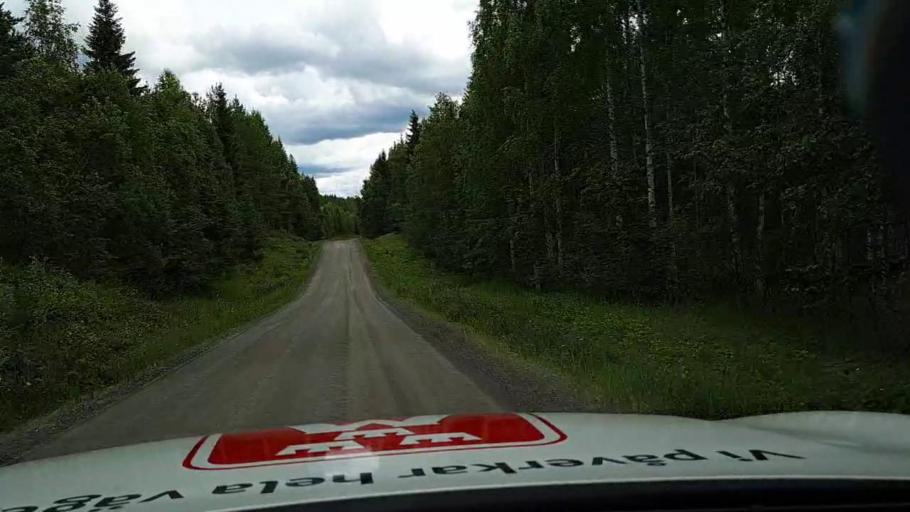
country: SE
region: Jaemtland
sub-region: Braecke Kommun
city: Braecke
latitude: 63.2151
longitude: 15.3628
